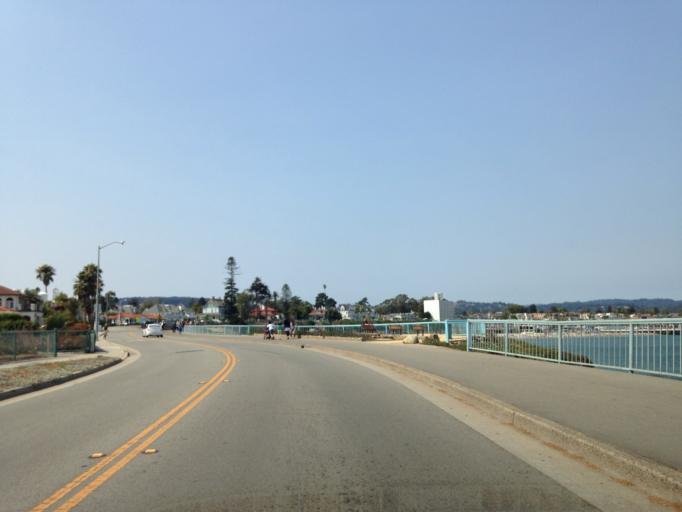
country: US
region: California
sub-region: Santa Cruz County
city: Santa Cruz
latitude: 36.9560
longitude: -122.0247
